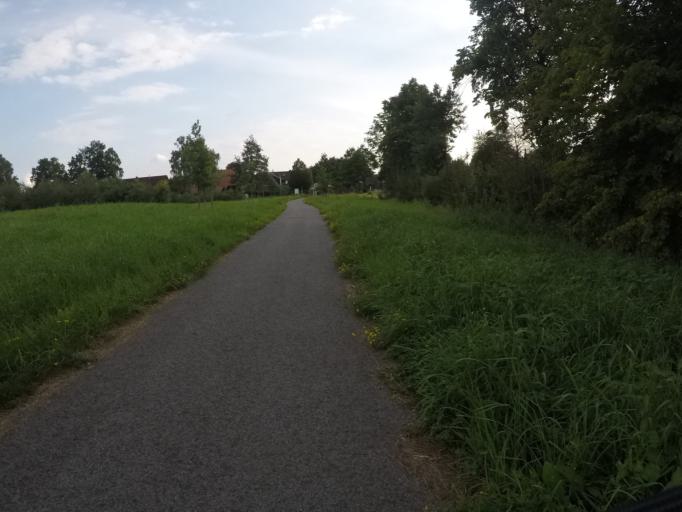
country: DE
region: North Rhine-Westphalia
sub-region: Regierungsbezirk Munster
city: Isselburg
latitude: 51.8193
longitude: 6.5201
